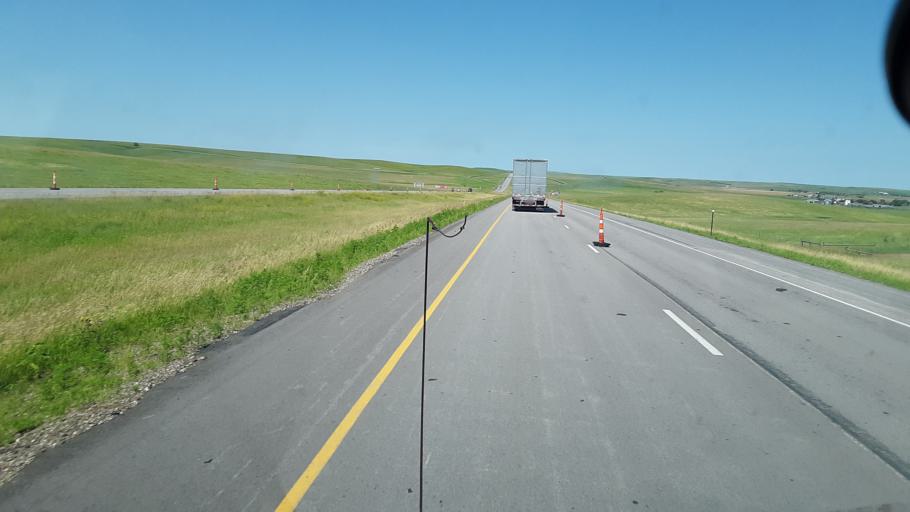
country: US
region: South Dakota
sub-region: Lyman County
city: Kennebec
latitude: 43.9130
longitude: -100.2654
